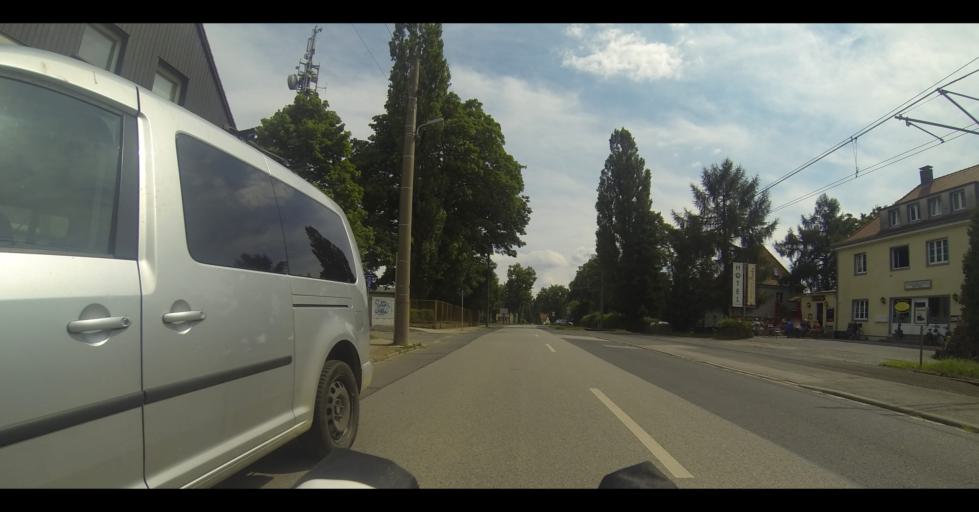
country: DE
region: Saxony
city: Albertstadt
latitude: 51.1135
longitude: 13.7493
